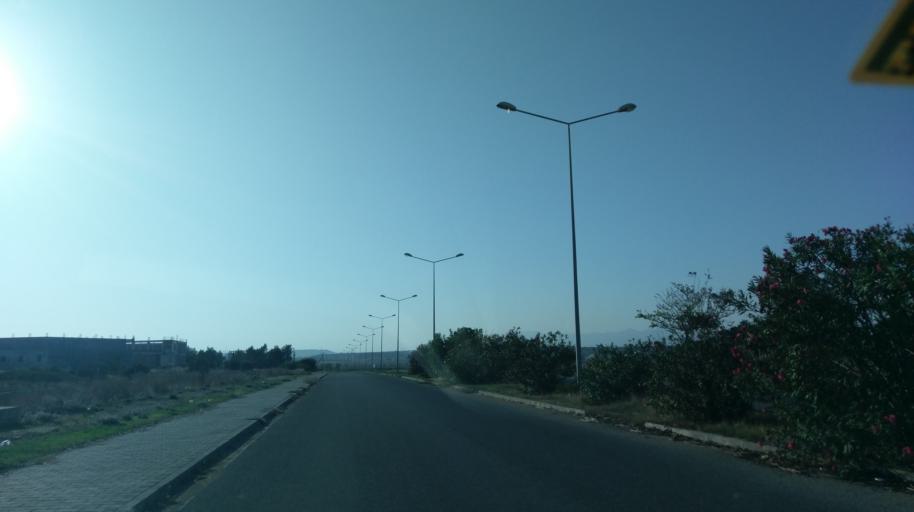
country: CY
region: Ammochostos
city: Leonarisso
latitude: 35.3717
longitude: 34.0816
